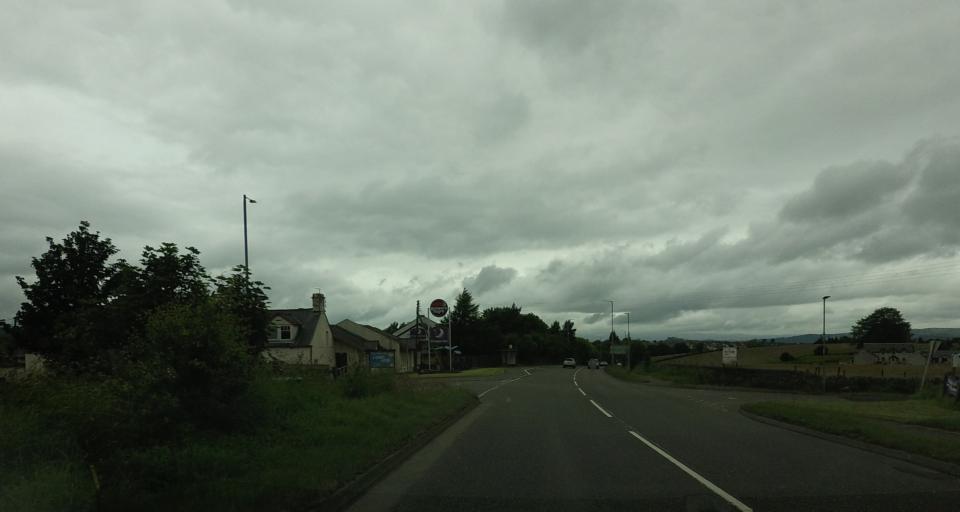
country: GB
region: Scotland
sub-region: Stirling
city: Bannockburn
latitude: 56.0808
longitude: -3.9240
